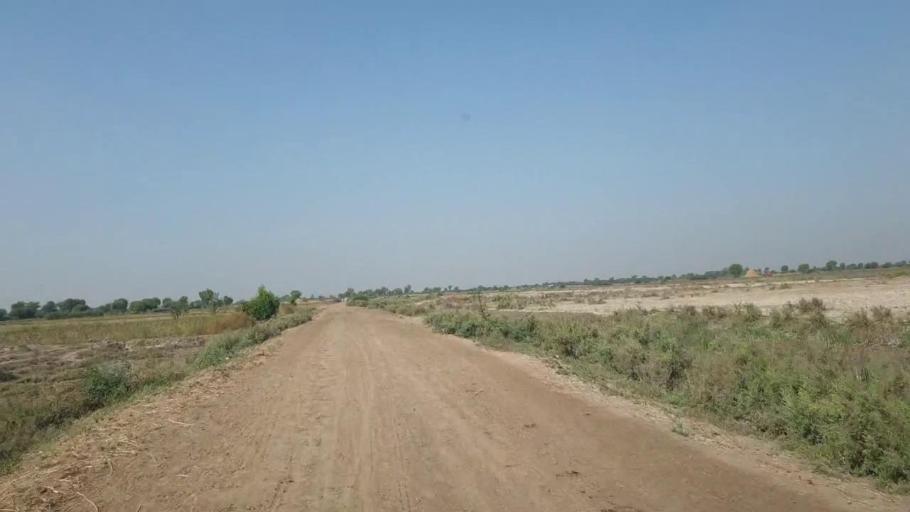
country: PK
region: Sindh
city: Badin
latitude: 24.5233
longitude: 68.7554
